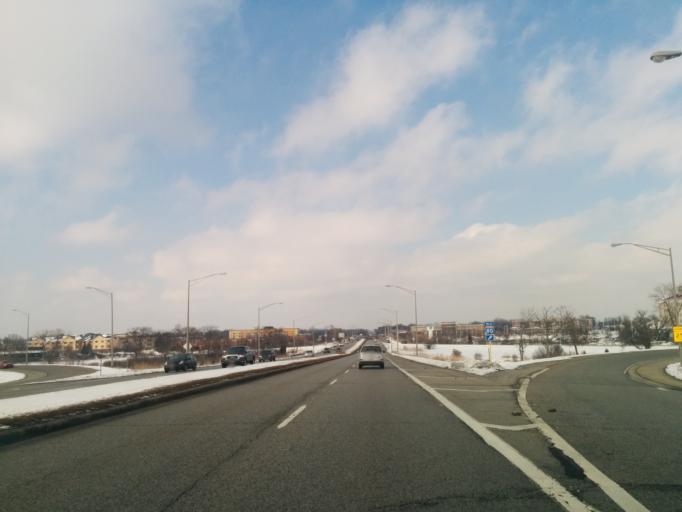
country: US
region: Illinois
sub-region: Cook County
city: Tinley Park
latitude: 41.5517
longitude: -87.7925
